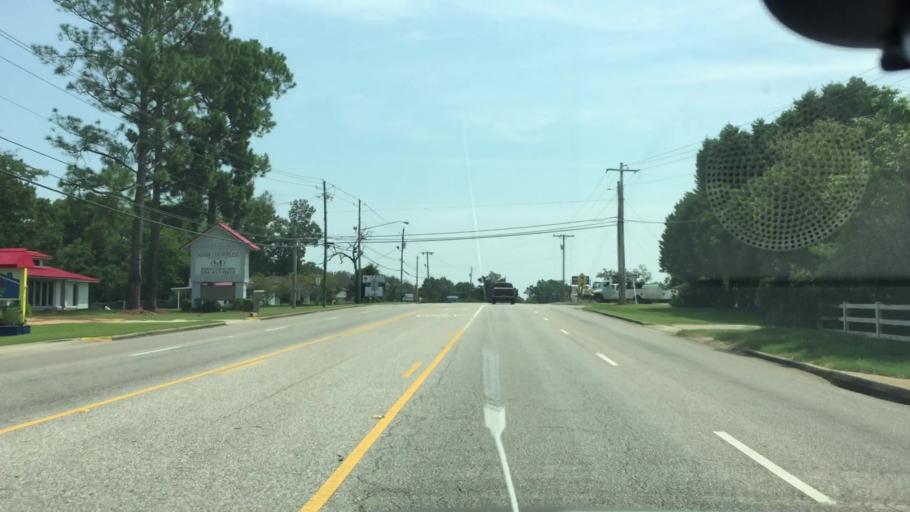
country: US
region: Alabama
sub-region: Coffee County
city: Enterprise
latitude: 31.3308
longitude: -85.8129
